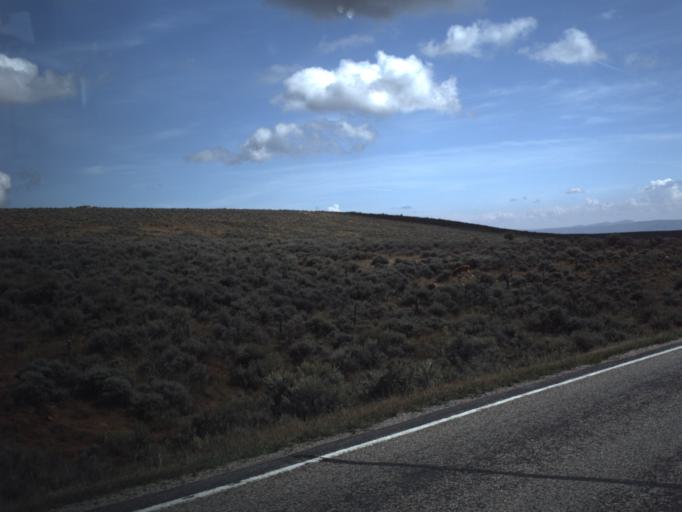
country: US
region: Utah
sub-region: Rich County
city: Randolph
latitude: 41.7969
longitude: -111.2355
